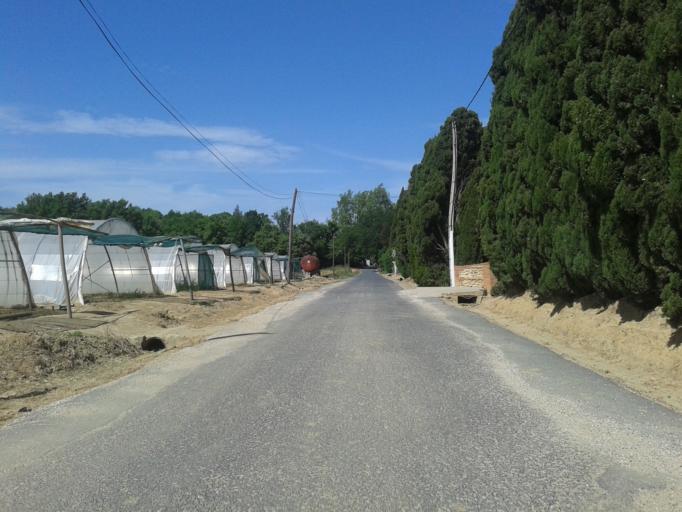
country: FR
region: Languedoc-Roussillon
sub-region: Departement des Pyrenees-Orientales
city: Corneilla-la-Riviere
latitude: 42.6996
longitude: 2.7342
